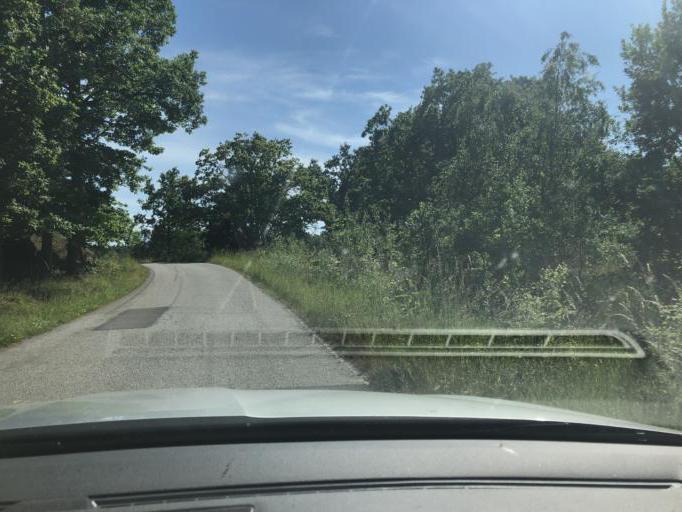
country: SE
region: Blekinge
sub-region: Karlshamns Kommun
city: Morrum
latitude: 56.1623
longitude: 14.8019
